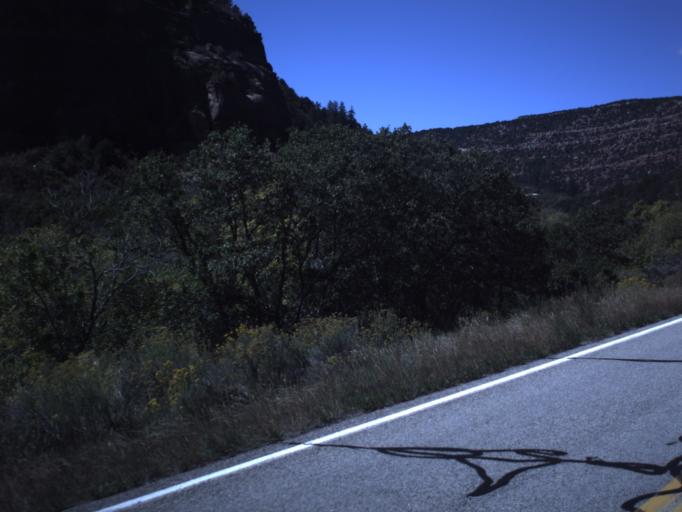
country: US
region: Utah
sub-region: San Juan County
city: Monticello
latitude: 38.3300
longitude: -109.0782
